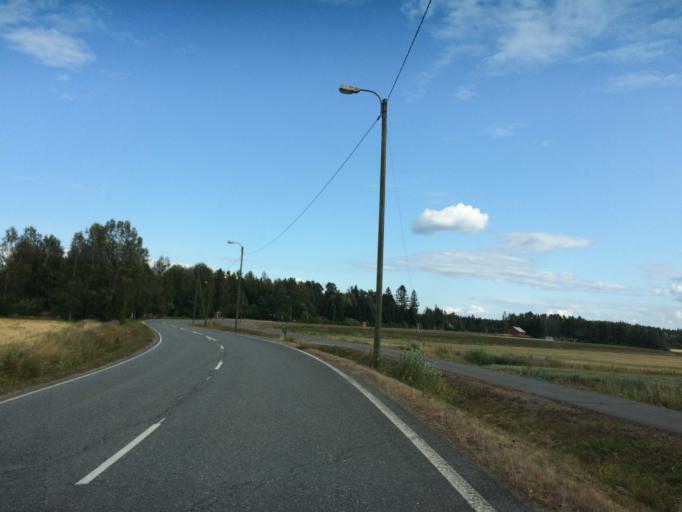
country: FI
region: Haeme
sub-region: Haemeenlinna
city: Tuulos
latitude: 61.0654
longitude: 24.6886
